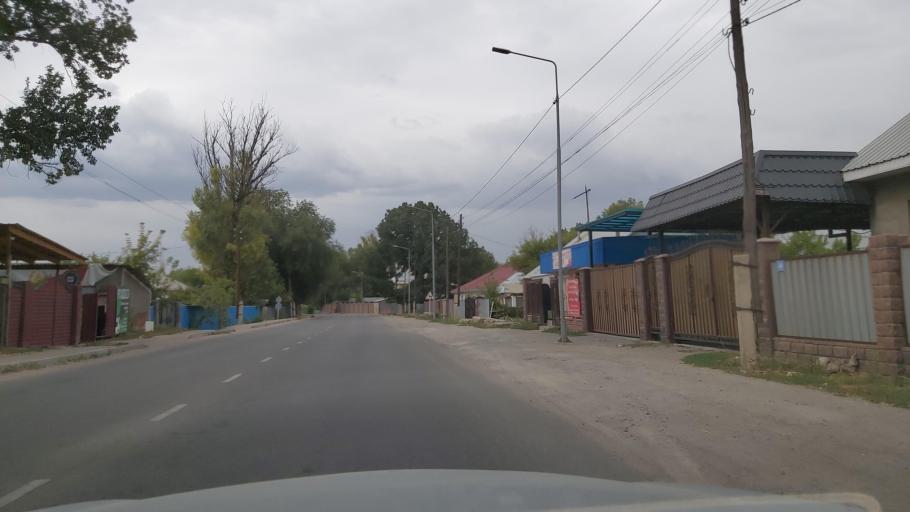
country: KZ
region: Almaty Oblysy
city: Energeticheskiy
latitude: 43.3860
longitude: 77.0780
